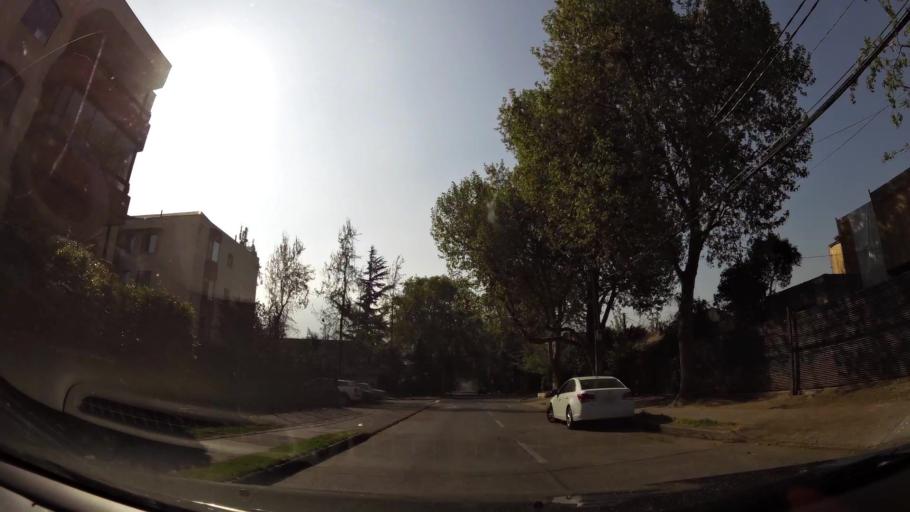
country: CL
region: Santiago Metropolitan
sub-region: Provincia de Santiago
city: Villa Presidente Frei, Nunoa, Santiago, Chile
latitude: -33.3826
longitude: -70.5501
